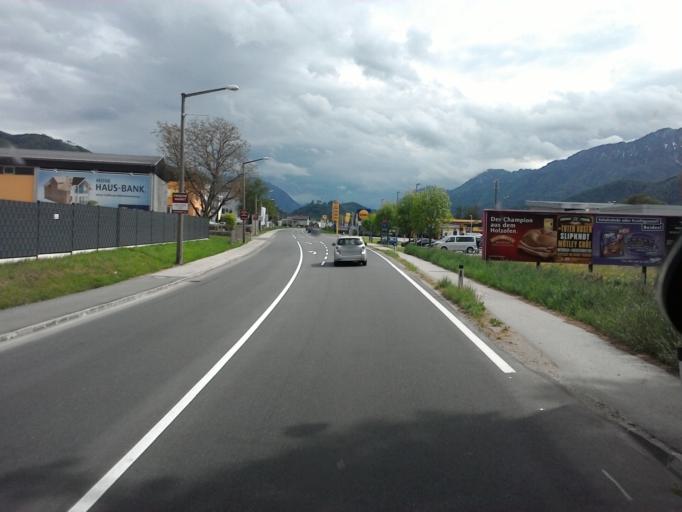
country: AT
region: Upper Austria
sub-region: Politischer Bezirk Kirchdorf an der Krems
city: Micheldorf in Oberoesterreich
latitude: 47.8985
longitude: 14.1266
